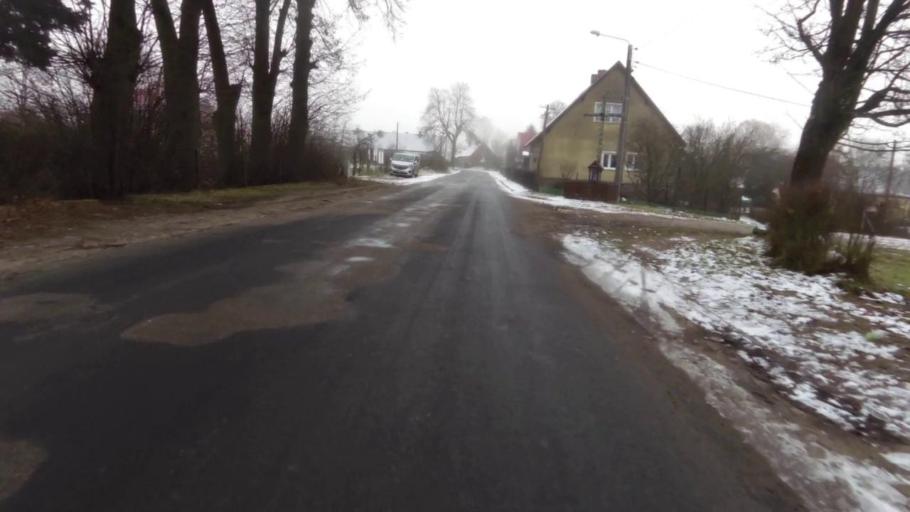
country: PL
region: West Pomeranian Voivodeship
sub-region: Powiat drawski
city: Wierzchowo
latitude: 53.4420
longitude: 16.1668
